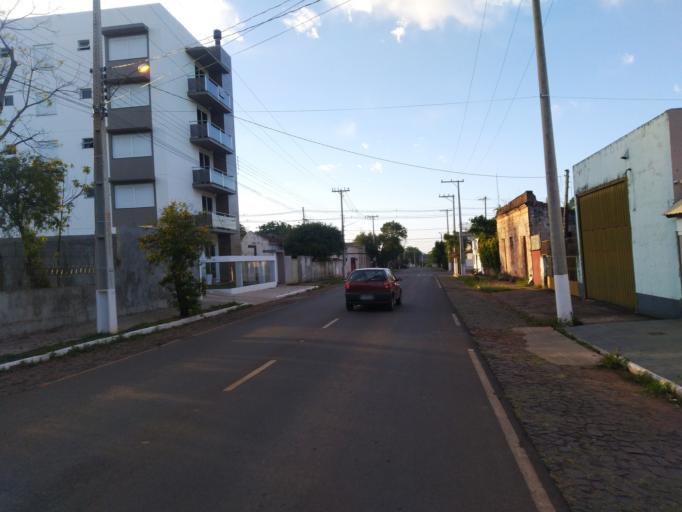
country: BR
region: Rio Grande do Sul
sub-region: Sao Borja
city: Sao Borja
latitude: -28.6634
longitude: -56.0084
